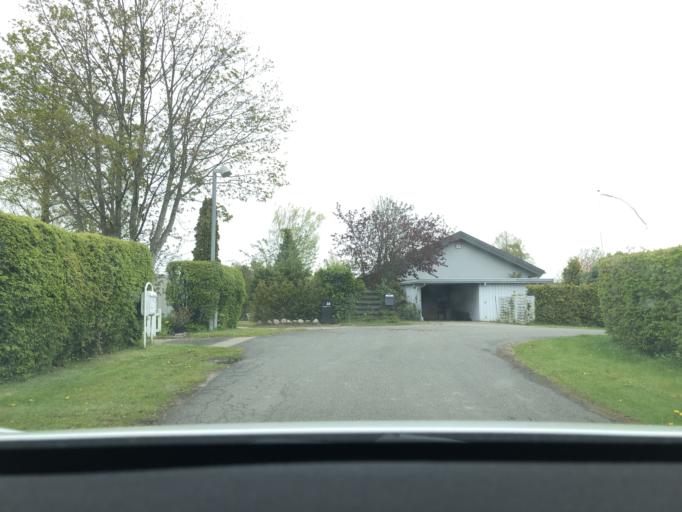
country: DK
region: Zealand
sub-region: Greve Kommune
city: Greve
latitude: 55.5706
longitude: 12.2752
